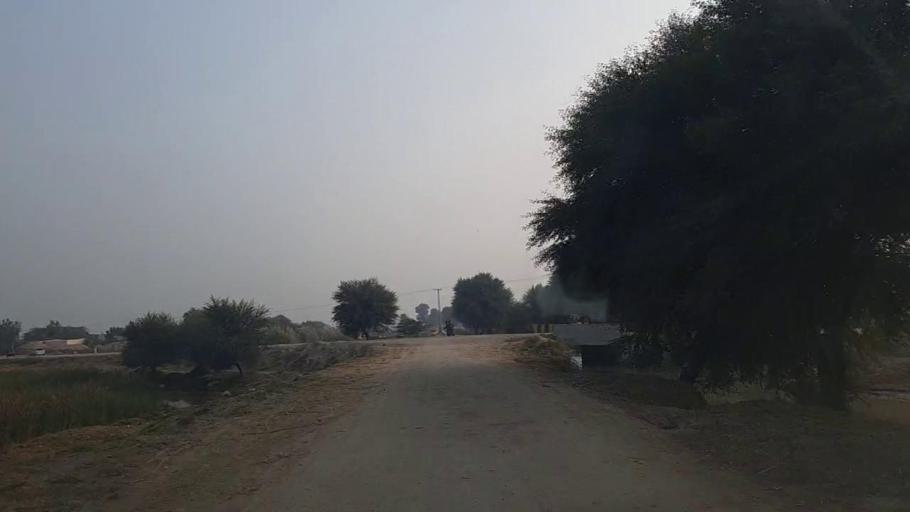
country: PK
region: Sindh
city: Sinjhoro
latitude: 26.1162
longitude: 68.8044
